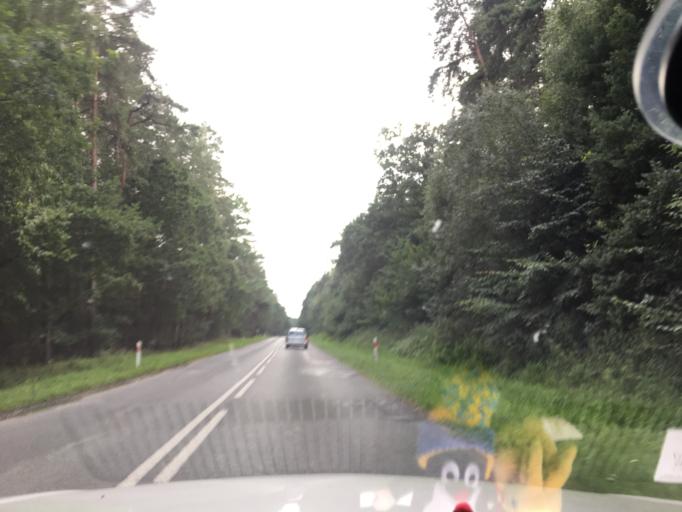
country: PL
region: West Pomeranian Voivodeship
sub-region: Powiat gryficki
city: Pobierowo
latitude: 54.0625
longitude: 14.9596
